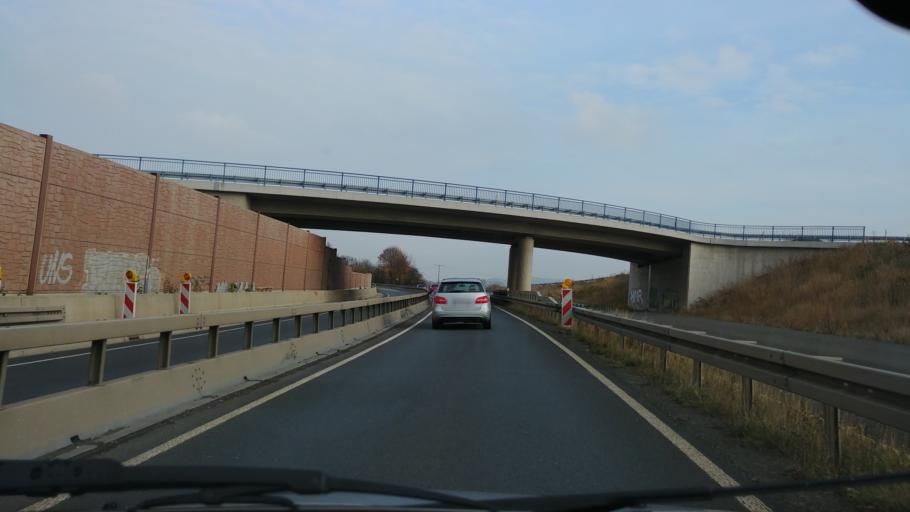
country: DE
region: Hesse
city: Oberbiel
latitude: 50.5493
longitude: 8.4307
